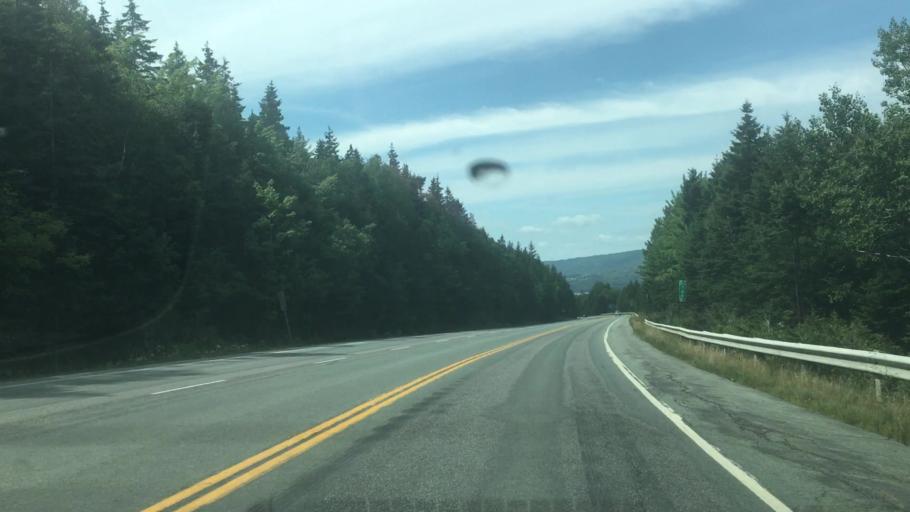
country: CA
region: Nova Scotia
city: Sydney Mines
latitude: 46.2467
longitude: -60.5533
